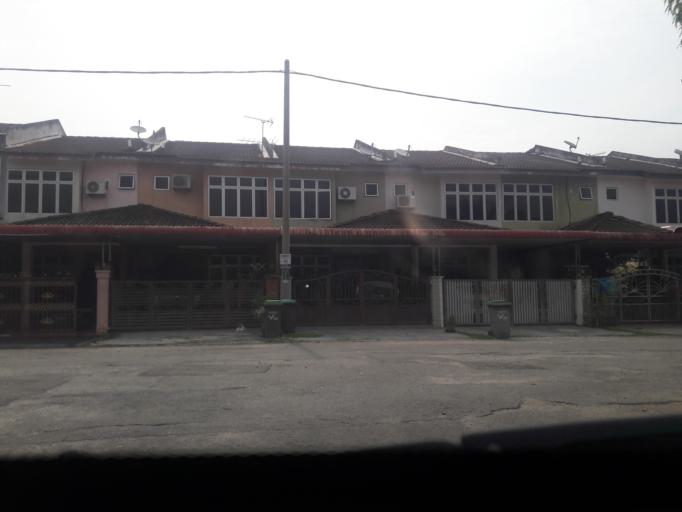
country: MY
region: Kedah
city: Kulim
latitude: 5.3653
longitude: 100.5387
